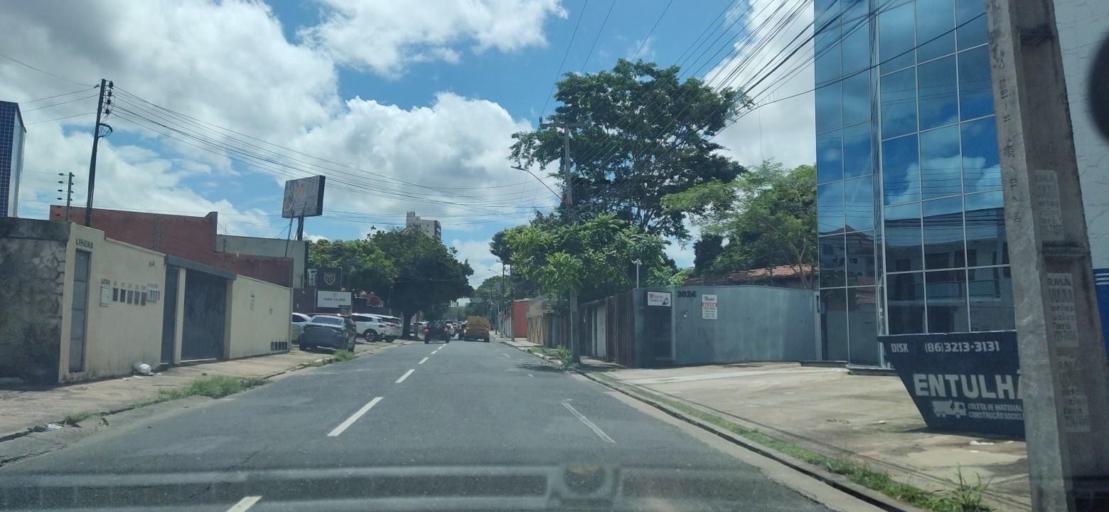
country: BR
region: Piaui
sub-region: Teresina
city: Teresina
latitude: -5.0645
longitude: -42.7861
